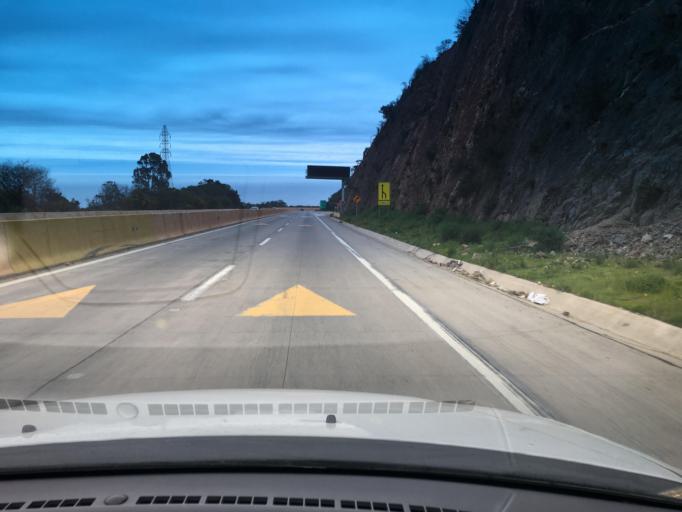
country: CL
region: Valparaiso
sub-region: Provincia de Valparaiso
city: Valparaiso
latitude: -33.0541
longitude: -71.6537
